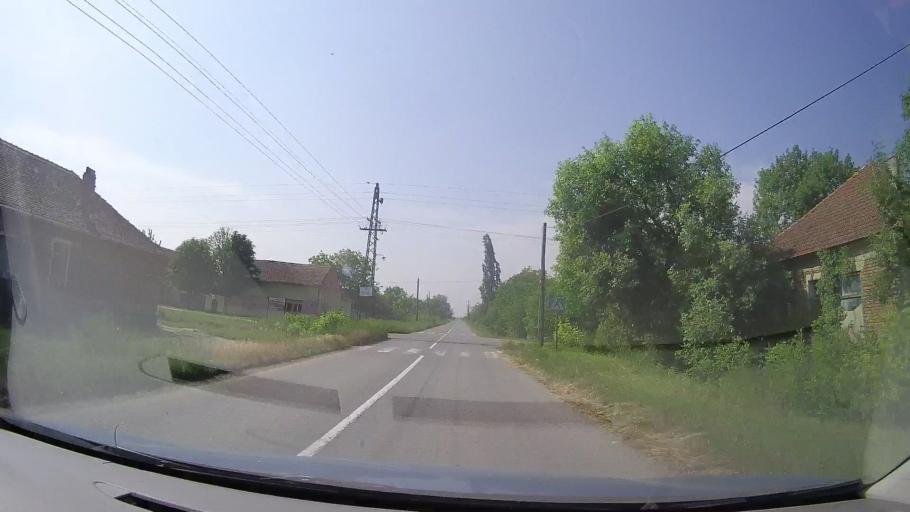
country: RS
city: Jarkovac
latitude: 45.2685
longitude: 20.7643
